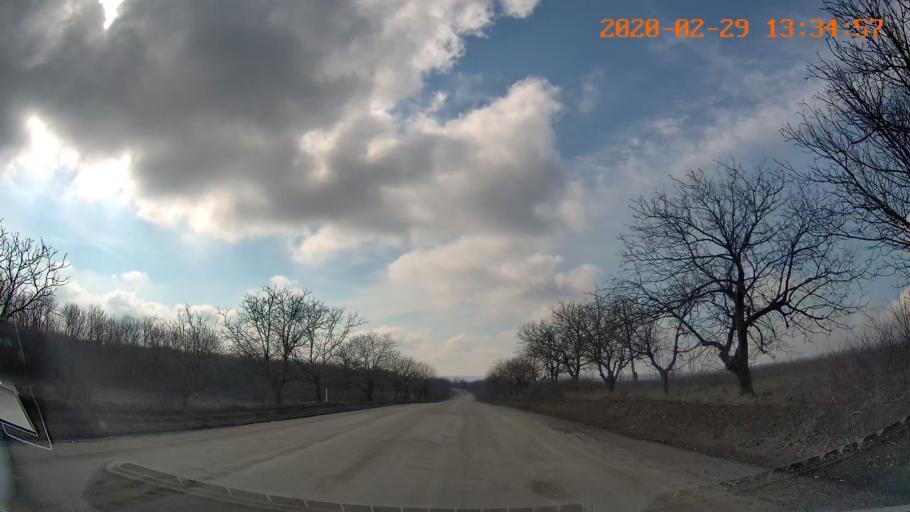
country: MD
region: Telenesti
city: Camenca
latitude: 47.8676
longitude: 28.6187
